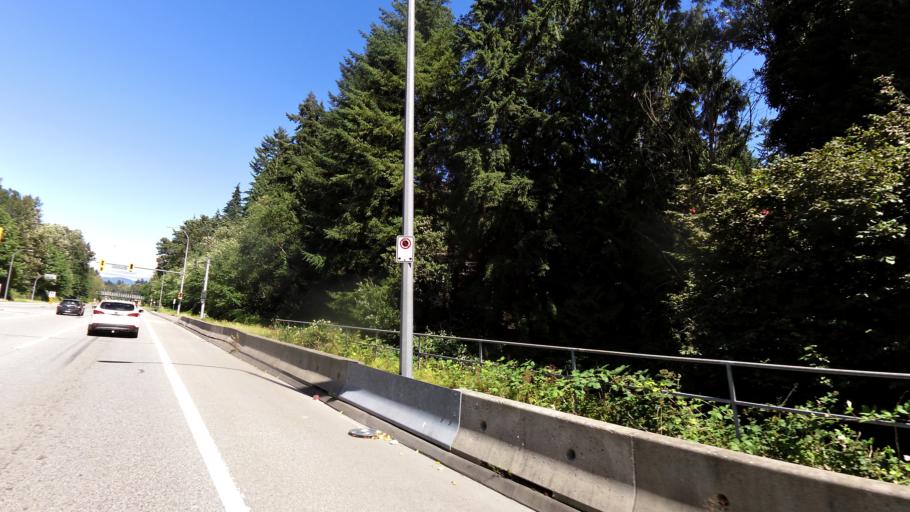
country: CA
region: British Columbia
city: Burnaby
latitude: 49.2596
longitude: -122.9095
